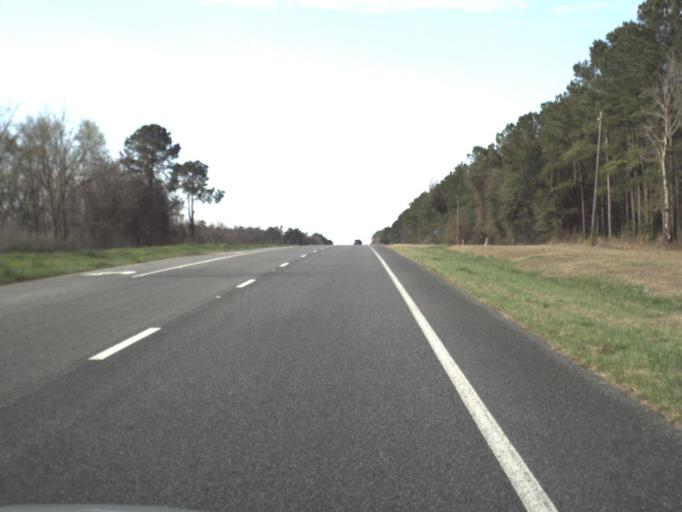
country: US
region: Florida
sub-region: Jefferson County
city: Monticello
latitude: 30.6372
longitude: -83.8735
